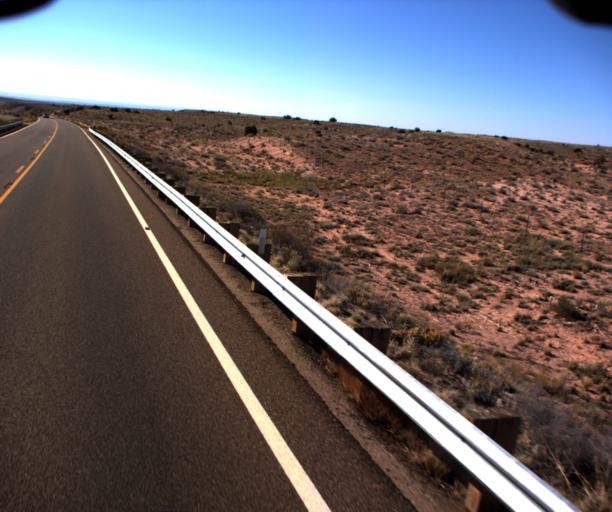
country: US
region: Arizona
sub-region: Navajo County
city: Dilkon
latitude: 35.1882
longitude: -110.4425
